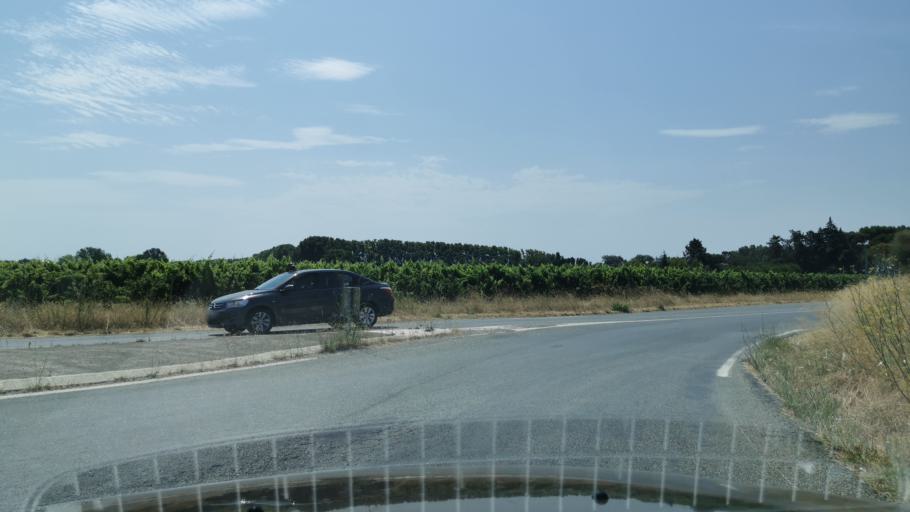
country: FR
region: Languedoc-Roussillon
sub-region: Departement de l'Aude
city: Argeliers
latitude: 43.2870
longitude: 2.9038
